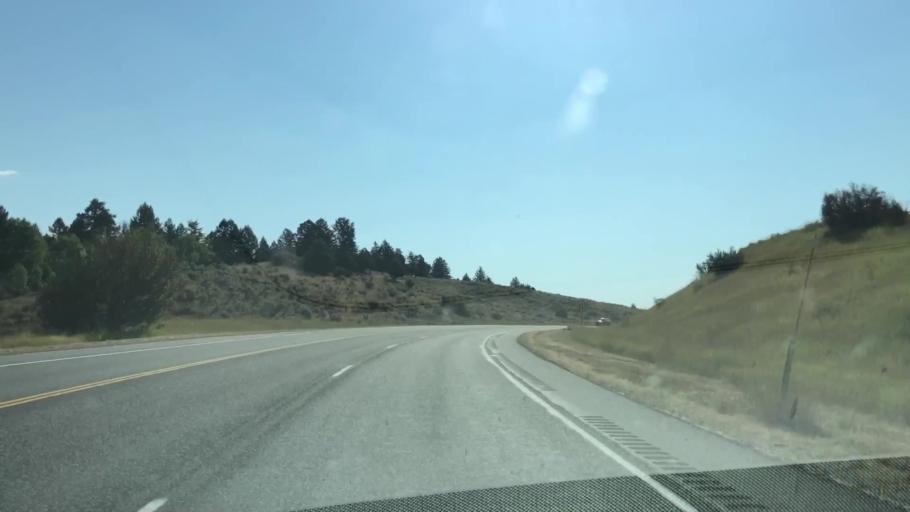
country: US
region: Idaho
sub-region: Teton County
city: Victor
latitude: 43.4565
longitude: -111.4092
